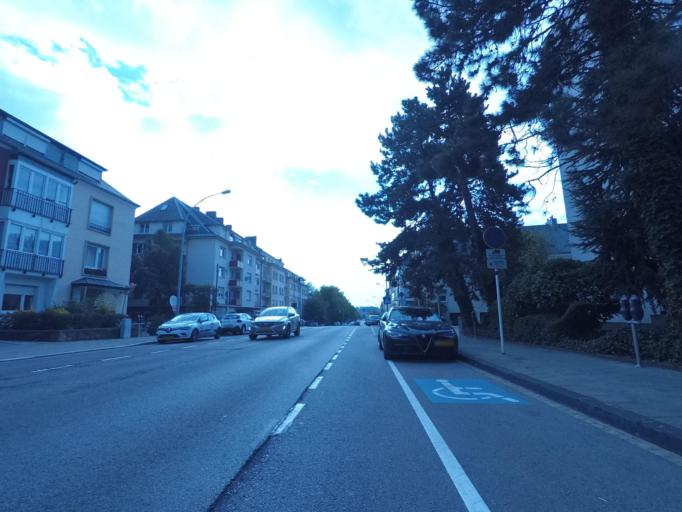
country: LU
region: Luxembourg
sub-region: Canton de Luxembourg
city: Luxembourg
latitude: 49.6067
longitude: 6.1097
